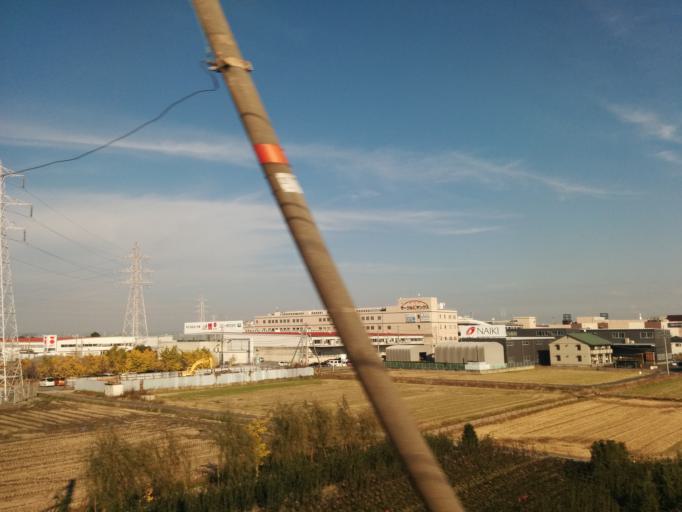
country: JP
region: Aichi
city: Inazawa
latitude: 35.2502
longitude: 136.7686
